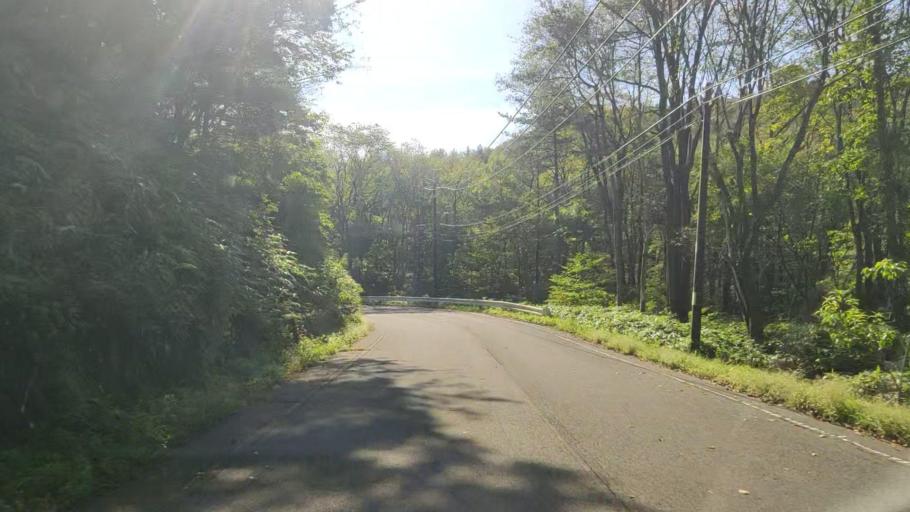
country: JP
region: Gunma
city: Nakanojomachi
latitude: 36.6059
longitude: 138.6800
